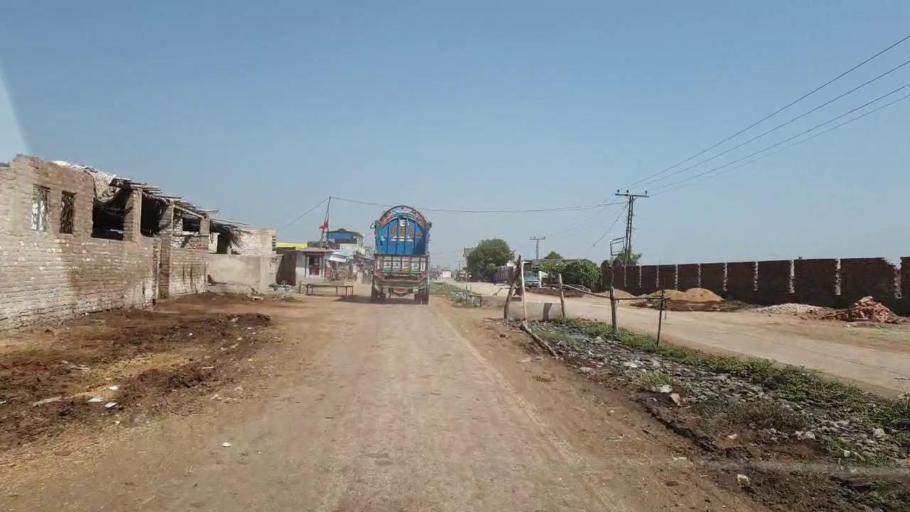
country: PK
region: Sindh
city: Hyderabad
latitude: 25.4243
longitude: 68.3914
